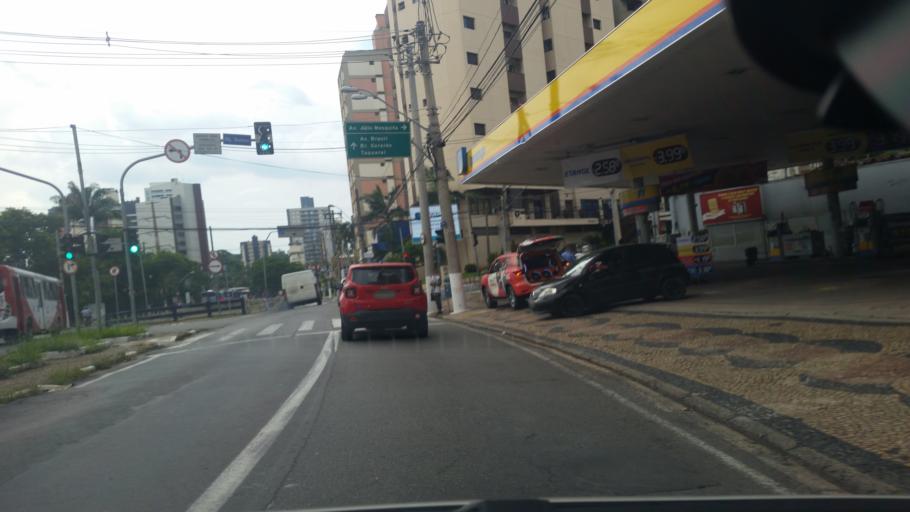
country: BR
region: Sao Paulo
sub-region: Campinas
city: Campinas
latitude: -22.8969
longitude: -47.0586
